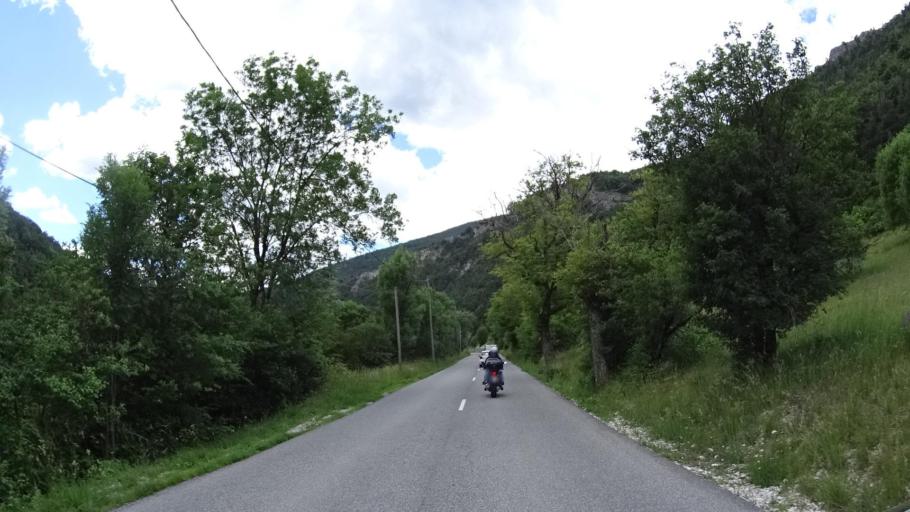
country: FR
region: Provence-Alpes-Cote d'Azur
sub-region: Departement des Alpes-de-Haute-Provence
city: Annot
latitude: 44.0325
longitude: 6.5592
